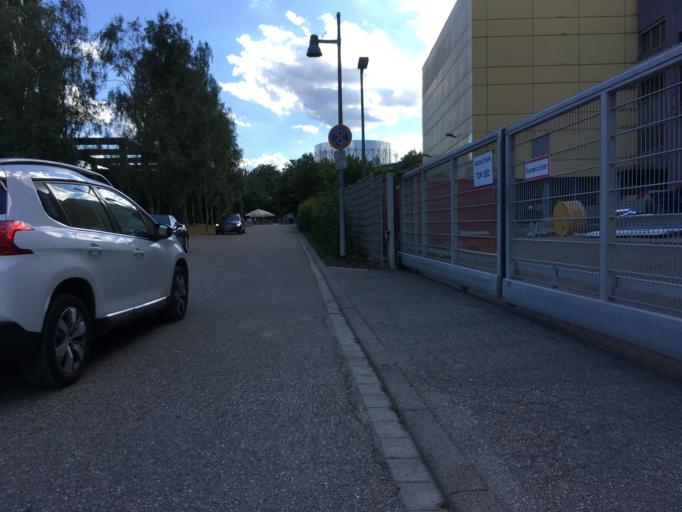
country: DE
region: Baden-Wuerttemberg
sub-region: Karlsruhe Region
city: Eutingen
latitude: 48.8965
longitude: 8.7253
